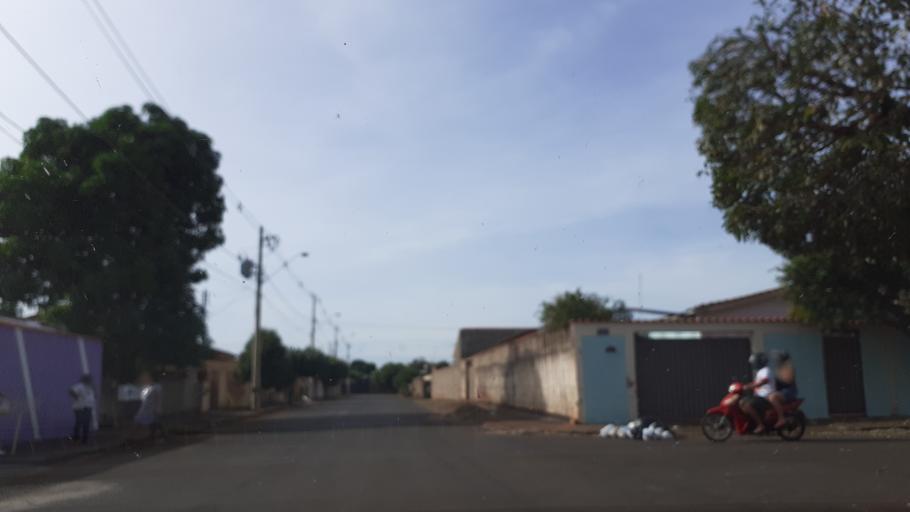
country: BR
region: Goias
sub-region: Itumbiara
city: Itumbiara
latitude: -18.4166
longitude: -49.2426
